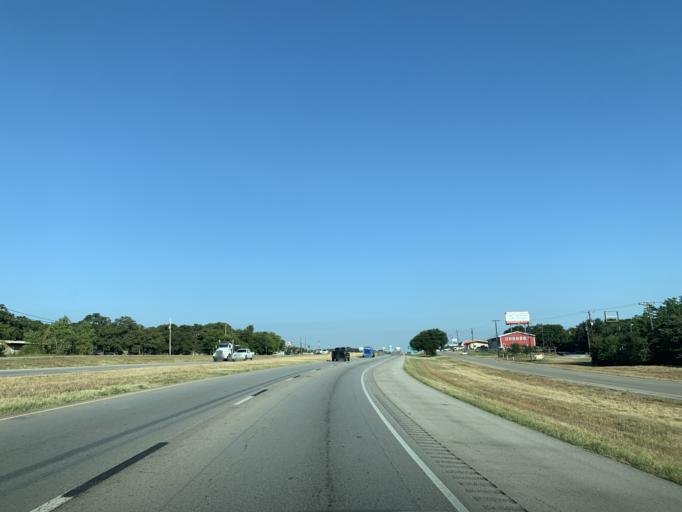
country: US
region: Texas
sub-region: Tarrant County
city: Lake Worth
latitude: 32.8203
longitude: -97.4643
